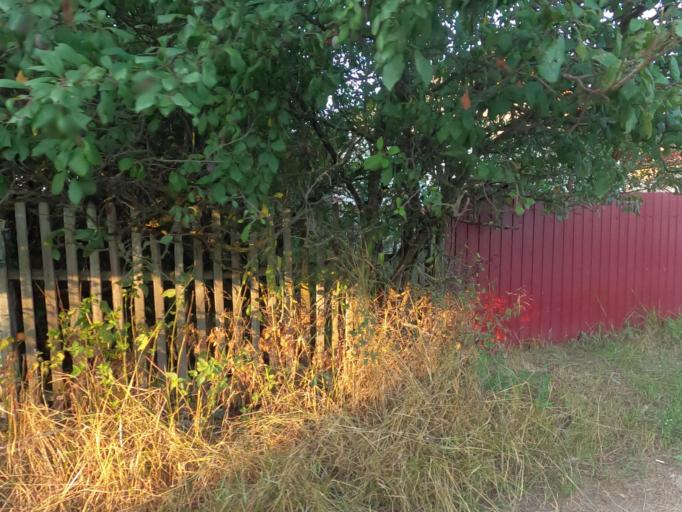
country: RU
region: Moskovskaya
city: Beloozerskiy
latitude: 55.4370
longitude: 38.4818
